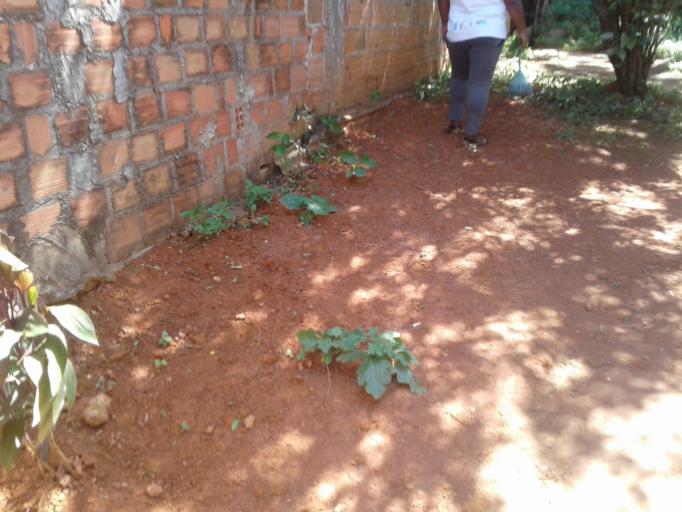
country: BR
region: Bahia
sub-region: Salvador
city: Salvador
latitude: -12.9102
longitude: -38.4695
